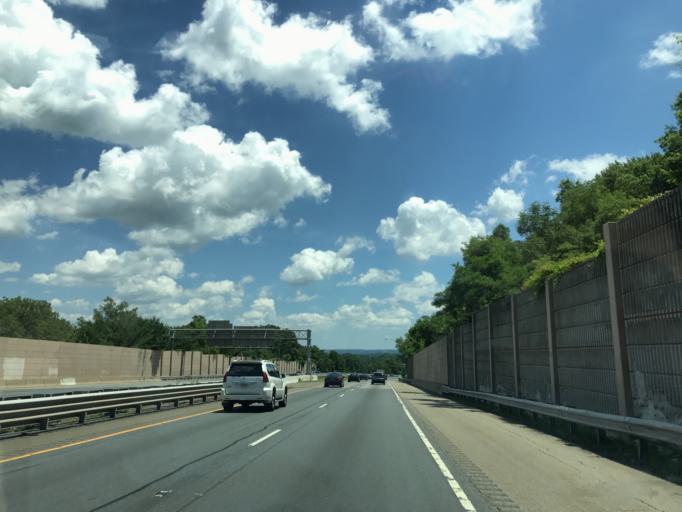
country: US
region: New Jersey
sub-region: Morris County
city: Madison
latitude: 40.7965
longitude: -74.4359
